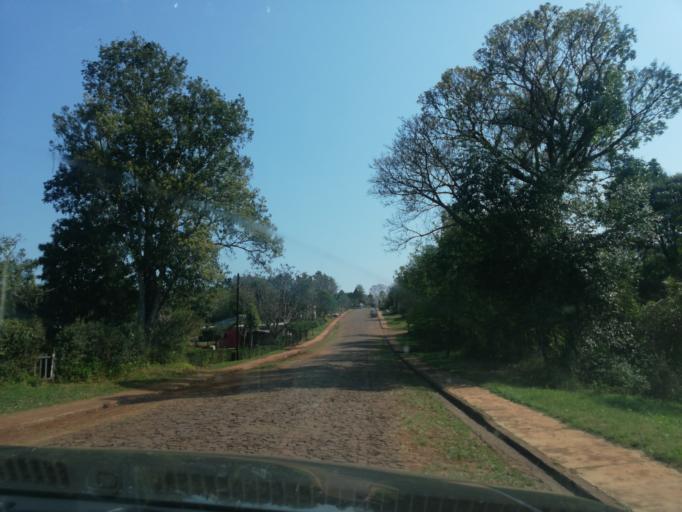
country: AR
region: Misiones
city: Bonpland
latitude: -27.4827
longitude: -55.4813
